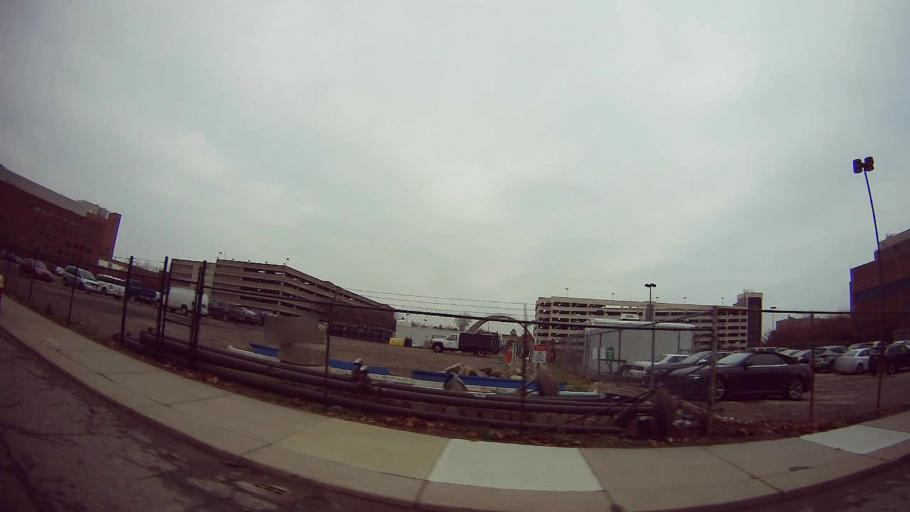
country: US
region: Michigan
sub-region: Wayne County
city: Detroit
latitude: 42.3556
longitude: -83.0578
